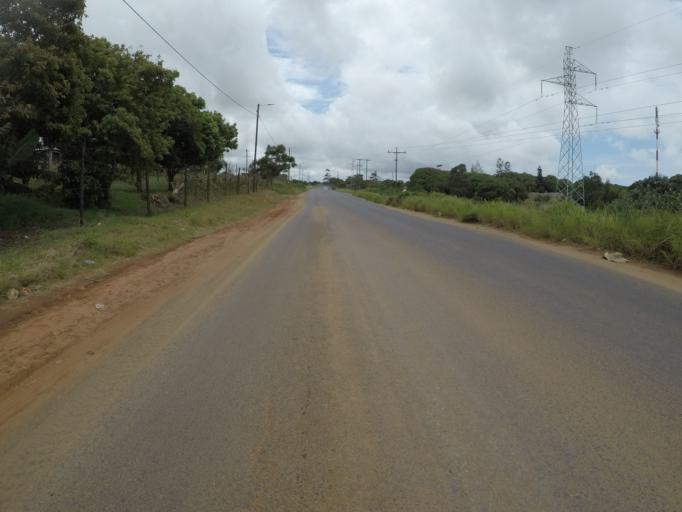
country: ZA
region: KwaZulu-Natal
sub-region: uThungulu District Municipality
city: eSikhawini
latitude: -28.8489
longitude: 31.9283
